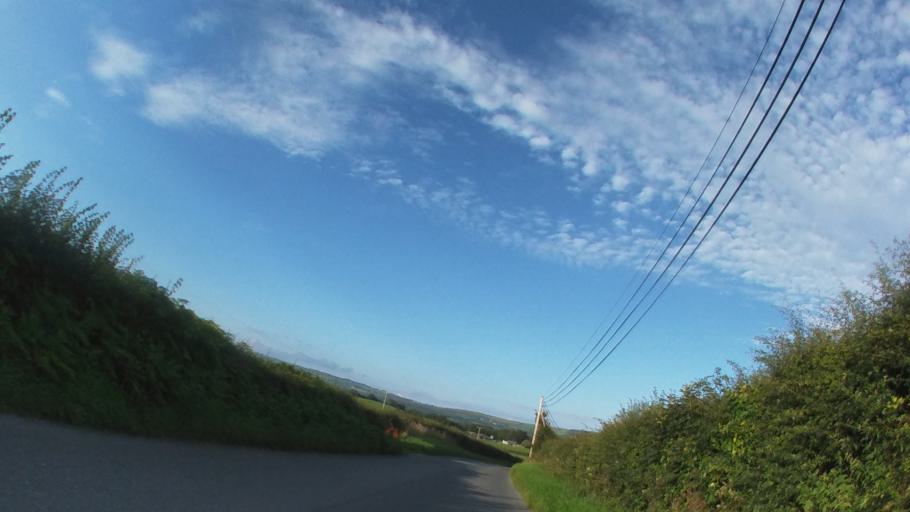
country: IE
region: Leinster
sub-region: Kilkenny
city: Kilkenny
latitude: 52.6747
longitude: -7.1995
